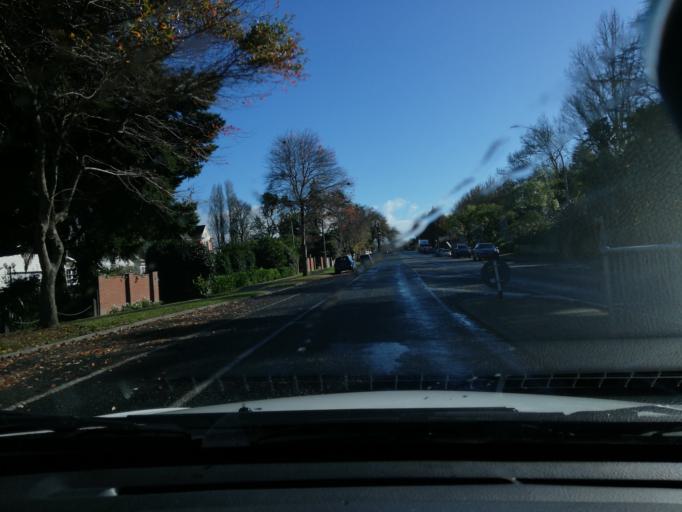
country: NZ
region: Waikato
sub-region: Hamilton City
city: Hamilton
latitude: -37.7726
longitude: 175.2726
